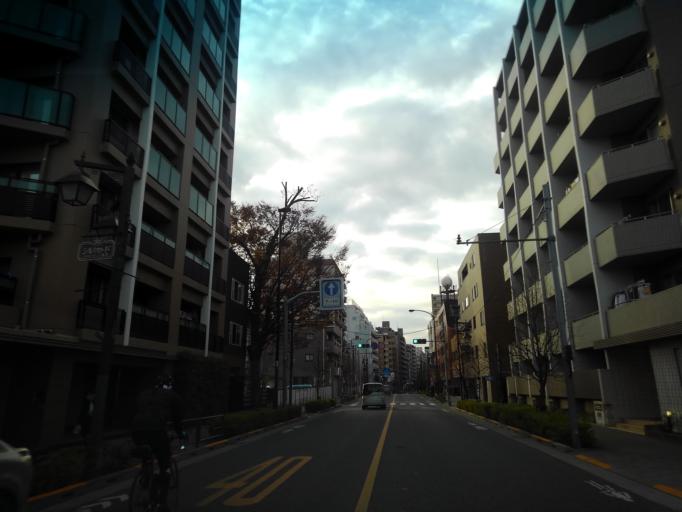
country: JP
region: Tokyo
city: Kokubunji
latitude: 35.7078
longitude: 139.5079
